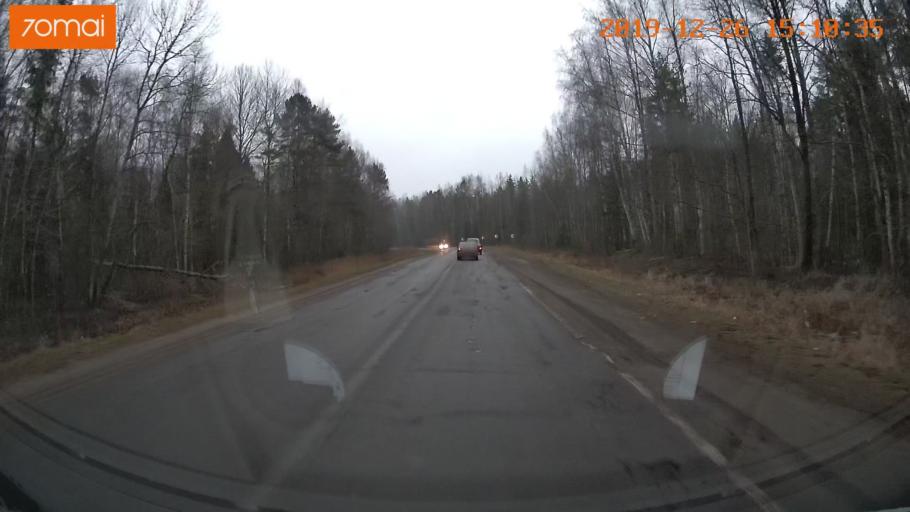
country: RU
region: Jaroslavl
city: Rybinsk
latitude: 58.1394
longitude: 38.8529
